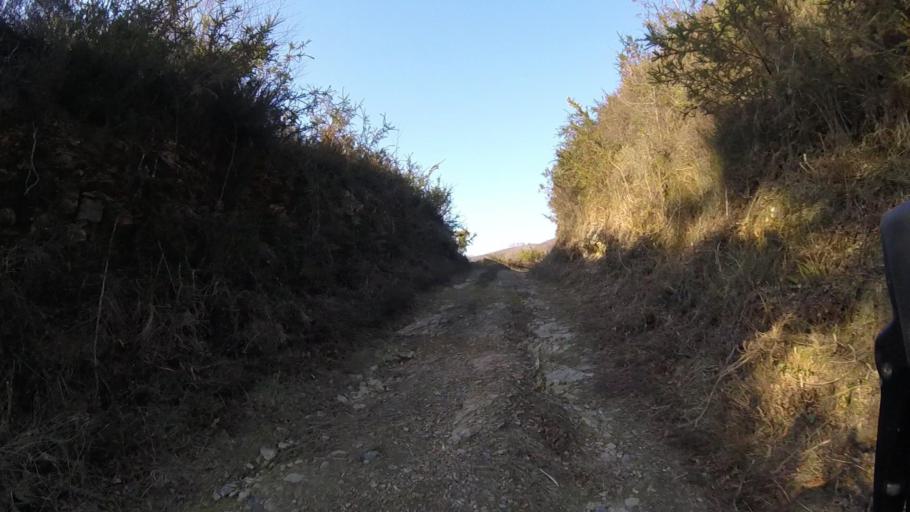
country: ES
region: Navarre
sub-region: Provincia de Navarra
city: Arano
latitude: 43.2185
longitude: -1.8632
